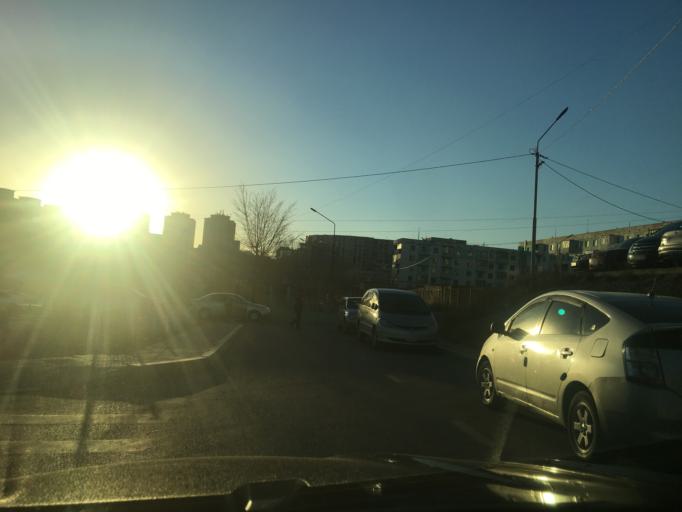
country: MN
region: Ulaanbaatar
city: Ulaanbaatar
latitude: 47.9254
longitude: 106.8876
